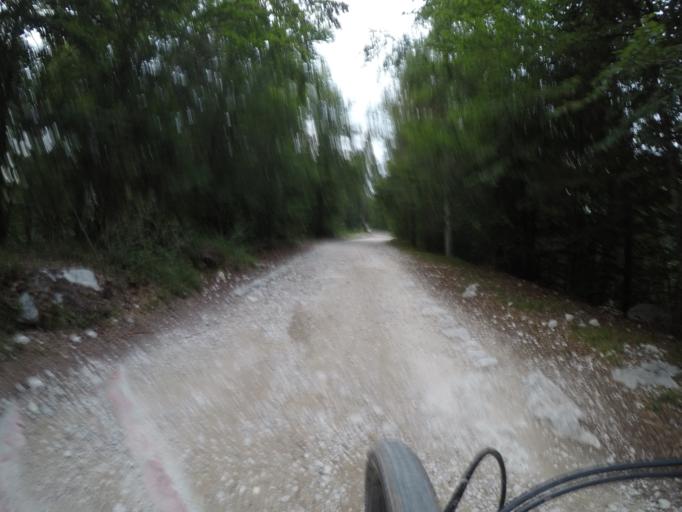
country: IT
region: Veneto
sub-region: Provincia di Vicenza
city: Gallio
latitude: 45.9049
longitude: 11.5251
